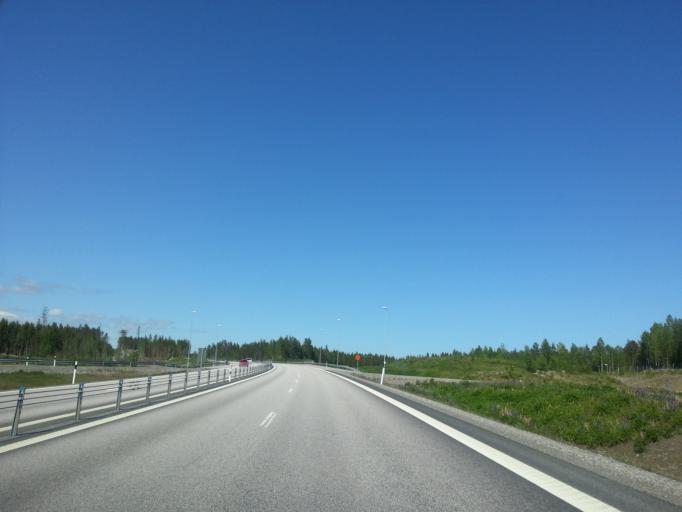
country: SE
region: Gaevleborg
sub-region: Hudiksvalls Kommun
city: Iggesund
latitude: 61.6073
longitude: 17.0107
